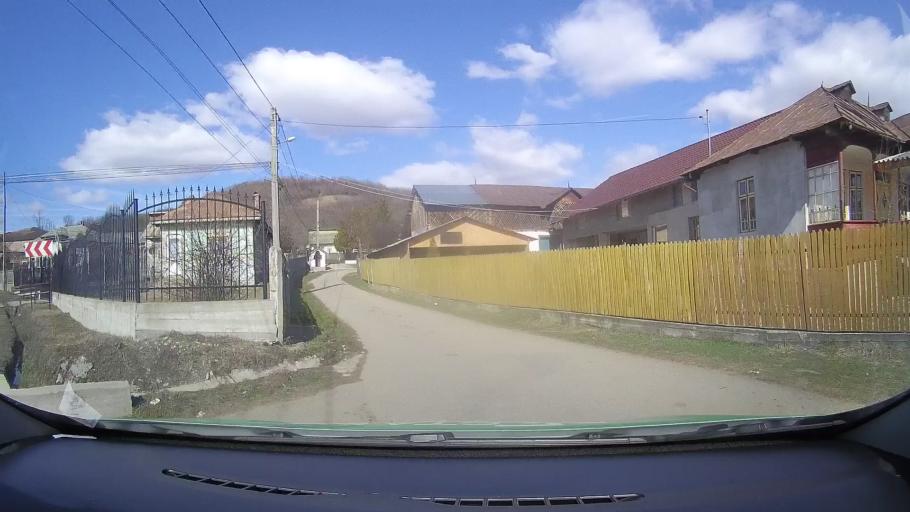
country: RO
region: Dambovita
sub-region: Comuna Glodeni
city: Glodeni
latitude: 45.0206
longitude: 25.4558
